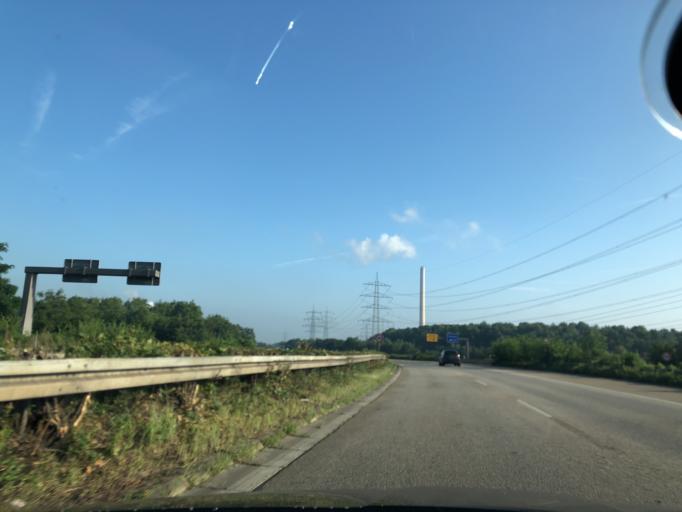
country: DE
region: North Rhine-Westphalia
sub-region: Regierungsbezirk Dusseldorf
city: Essen
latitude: 51.5044
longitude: 6.9969
